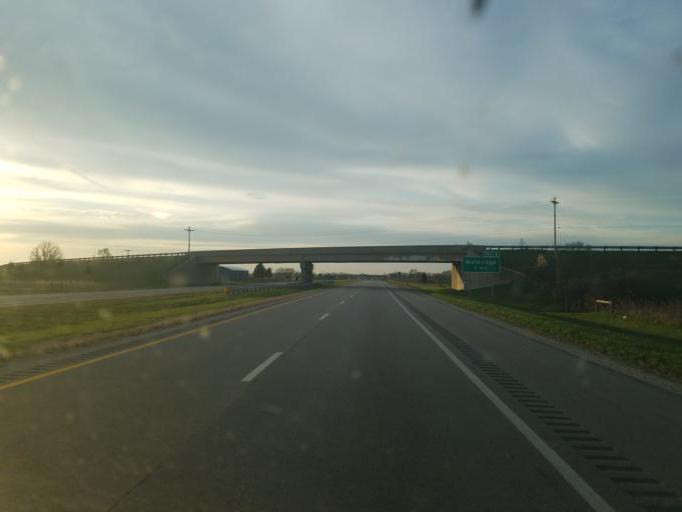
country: US
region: Ohio
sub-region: Wood County
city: Walbridge
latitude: 41.5724
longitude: -83.4675
